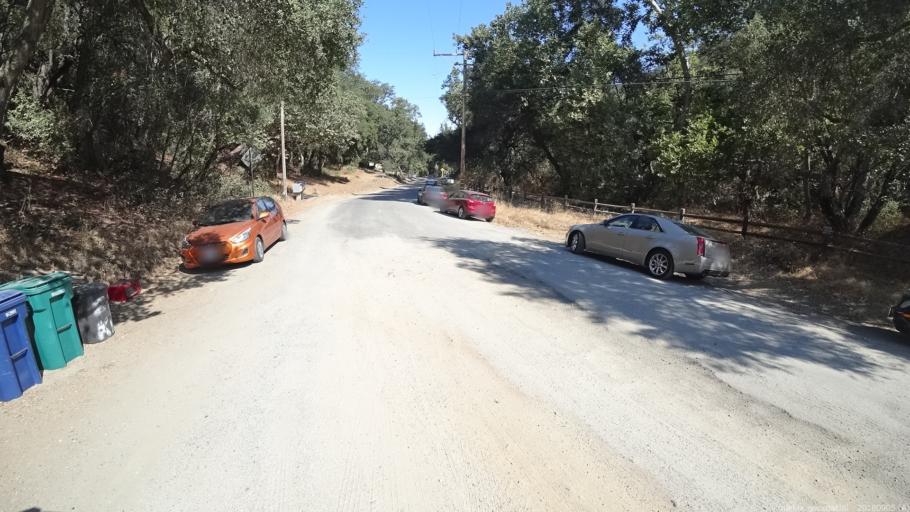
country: US
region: California
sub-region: Monterey County
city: Gonzales
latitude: 36.3691
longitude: -121.5904
